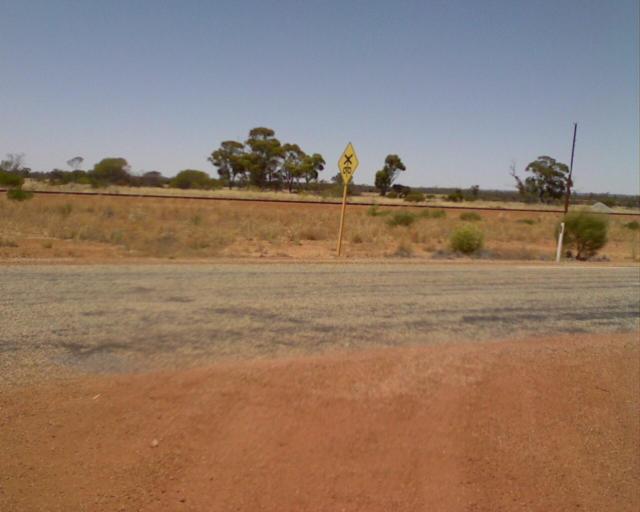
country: AU
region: Western Australia
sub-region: Merredin
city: Merredin
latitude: -30.8195
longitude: 117.9080
